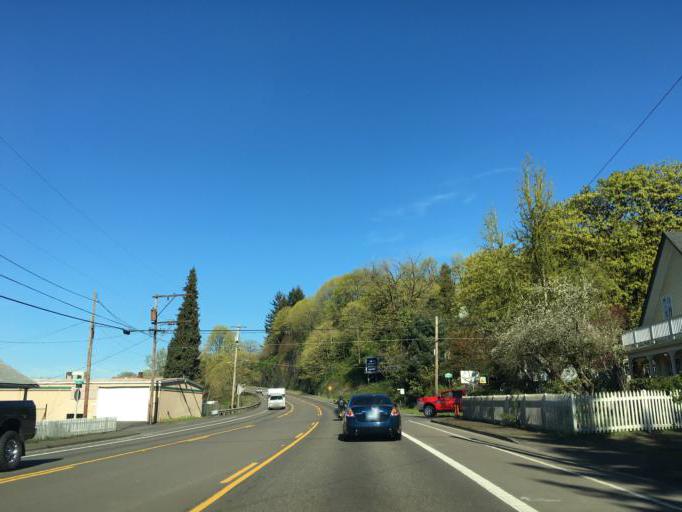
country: US
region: Oregon
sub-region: Clackamas County
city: Oregon City
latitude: 45.3472
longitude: -122.6216
